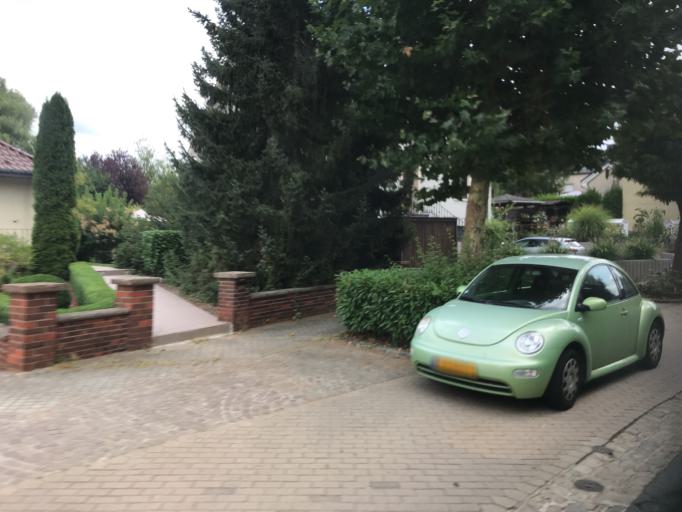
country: LU
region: Luxembourg
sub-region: Canton d'Esch-sur-Alzette
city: Bettembourg
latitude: 49.5242
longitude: 6.1259
